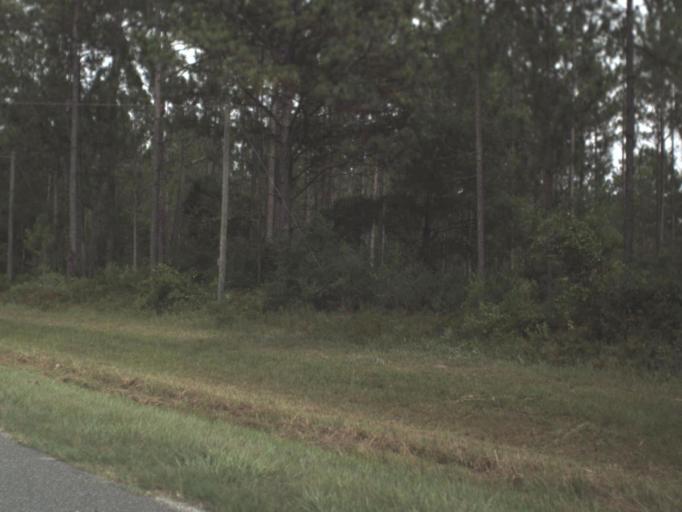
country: US
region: Florida
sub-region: Taylor County
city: Perry
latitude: 30.1013
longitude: -83.4455
